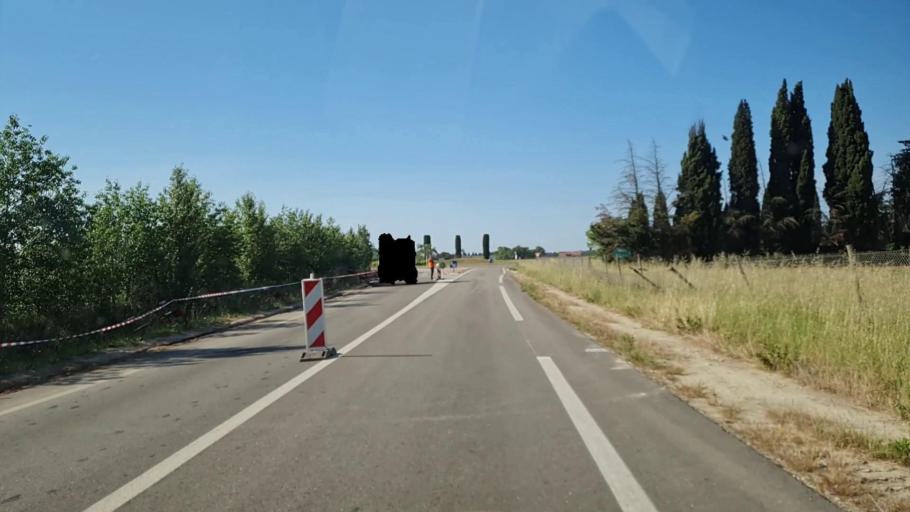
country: FR
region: Languedoc-Roussillon
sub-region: Departement du Gard
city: Garons
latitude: 43.7417
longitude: 4.4088
